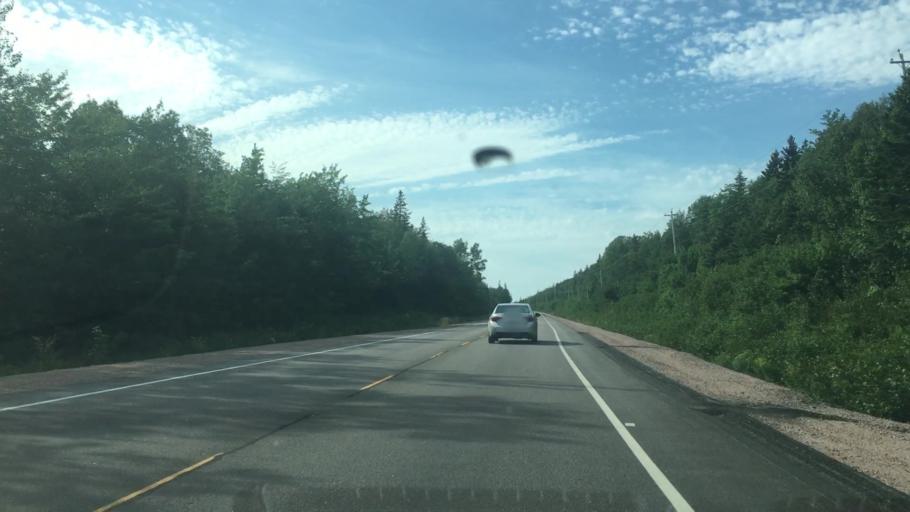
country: CA
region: Nova Scotia
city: Sydney Mines
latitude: 46.8155
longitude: -60.3421
